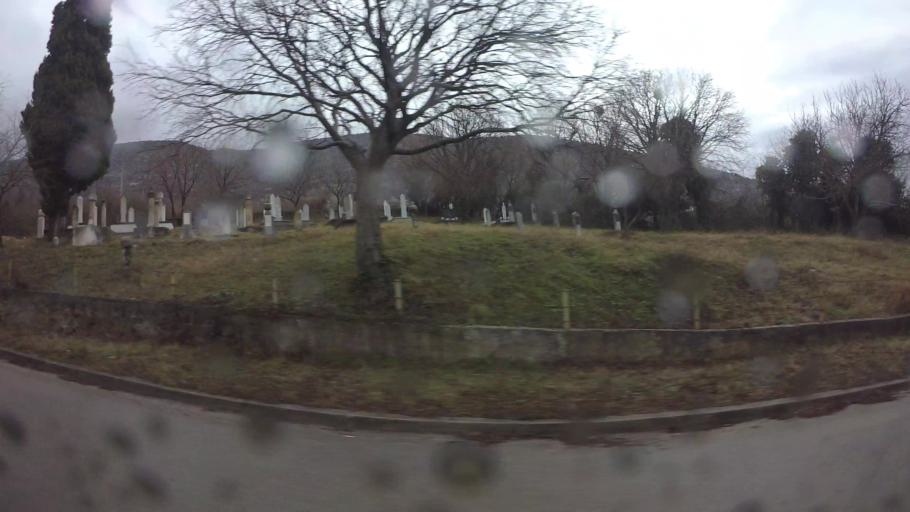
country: BA
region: Federation of Bosnia and Herzegovina
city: Blagaj
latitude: 43.2990
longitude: 17.8551
